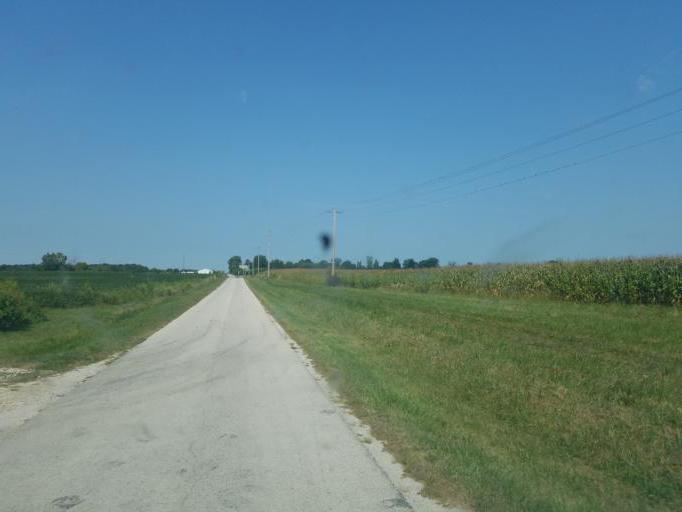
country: US
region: Ohio
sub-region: Crawford County
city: Bucyrus
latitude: 40.8126
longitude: -83.1121
